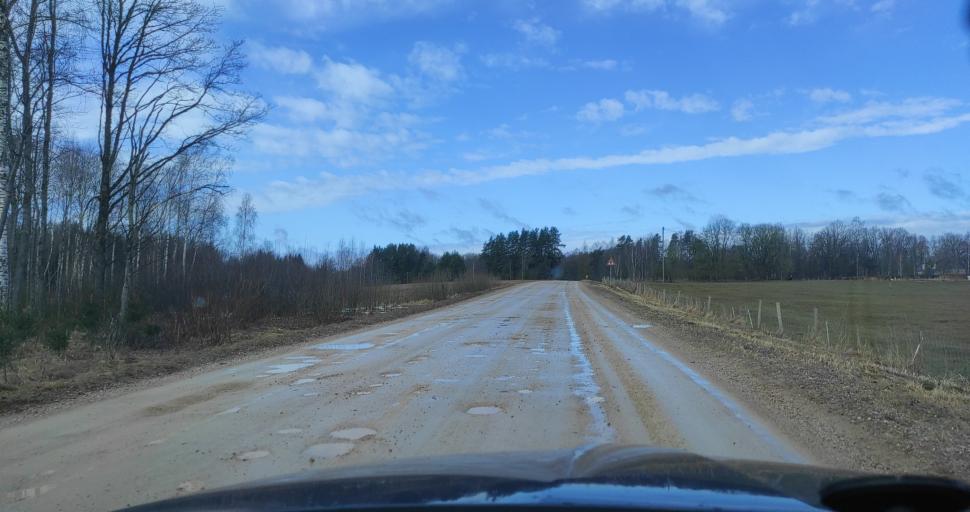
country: LV
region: Tukuma Rajons
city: Tukums
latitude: 57.1087
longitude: 23.0339
